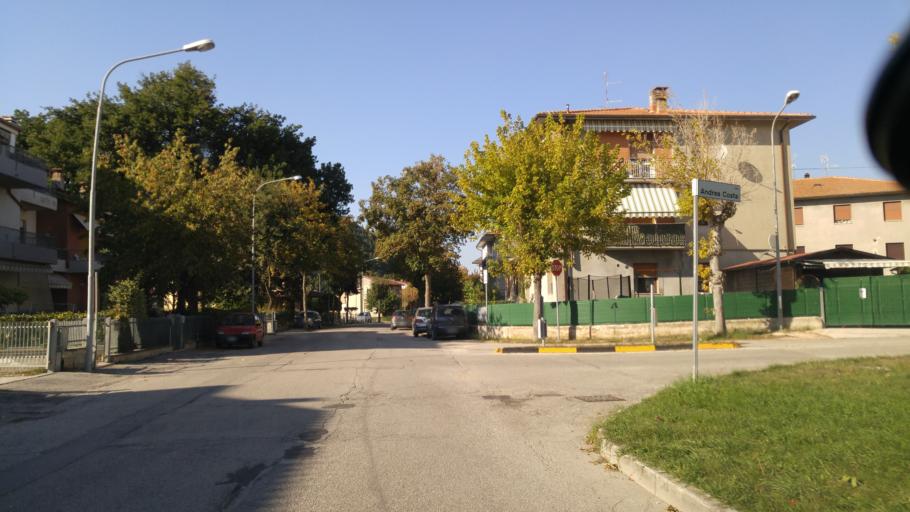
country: IT
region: The Marches
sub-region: Provincia di Pesaro e Urbino
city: Fermignano
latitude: 43.6691
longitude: 12.6441
